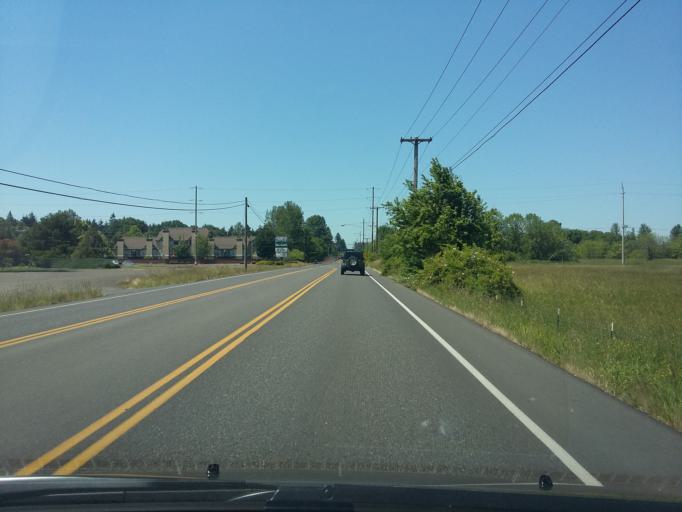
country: US
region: Washington
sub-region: Clark County
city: Walnut Grove
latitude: 45.6789
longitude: -122.5969
